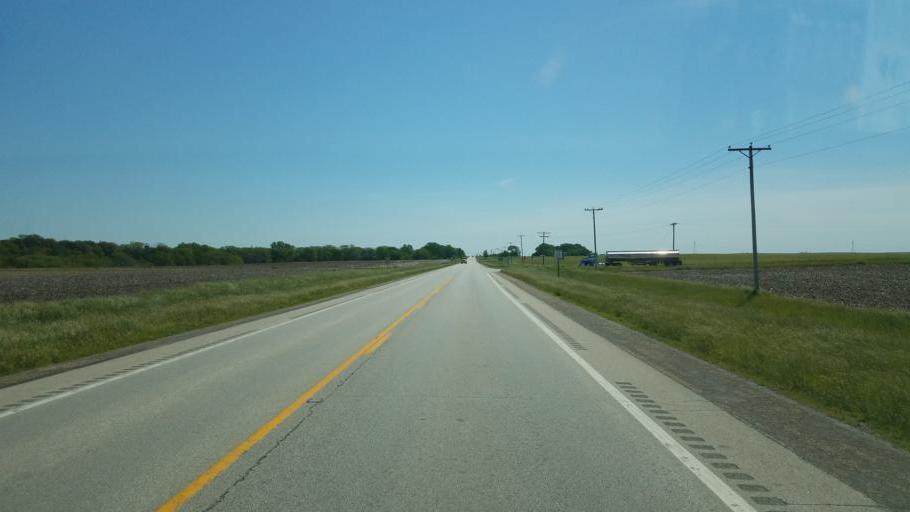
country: US
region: Illinois
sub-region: McLean County
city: Heyworth
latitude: 40.3122
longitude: -88.9612
